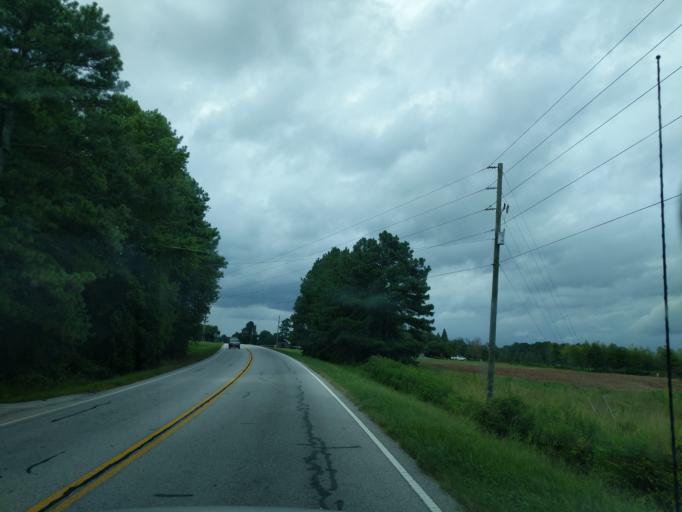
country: US
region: Georgia
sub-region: Walton County
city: Loganville
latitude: 33.7918
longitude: -83.9547
